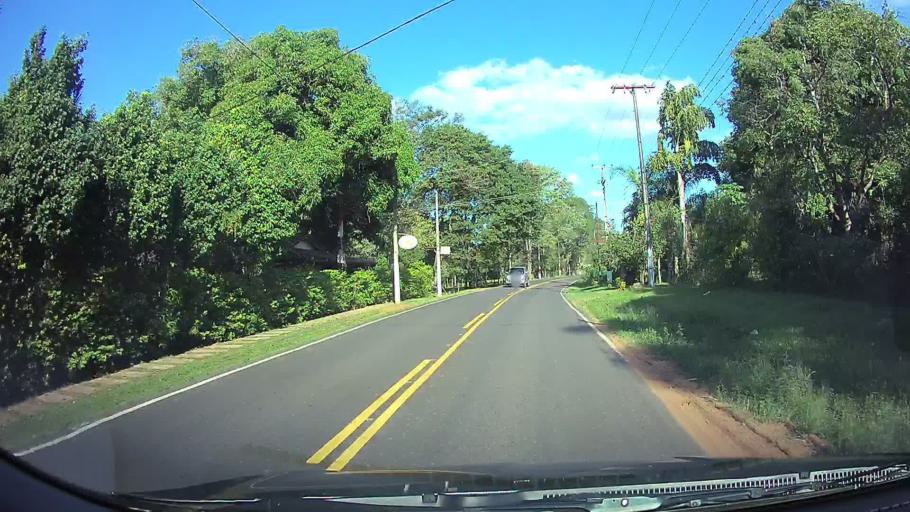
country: PY
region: Central
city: Aregua
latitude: -25.2853
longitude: -57.3963
